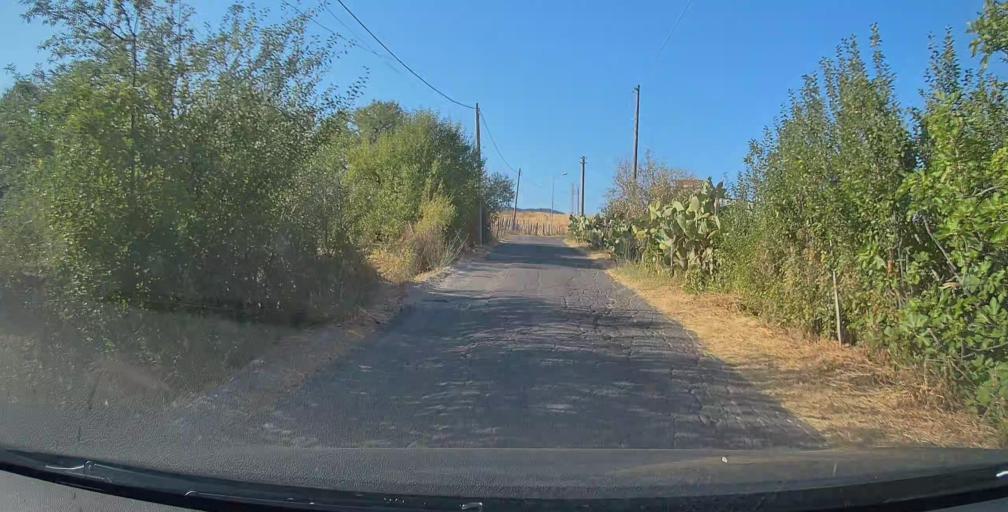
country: IT
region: Sicily
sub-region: Messina
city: San Piero Patti
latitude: 38.0739
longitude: 14.9856
